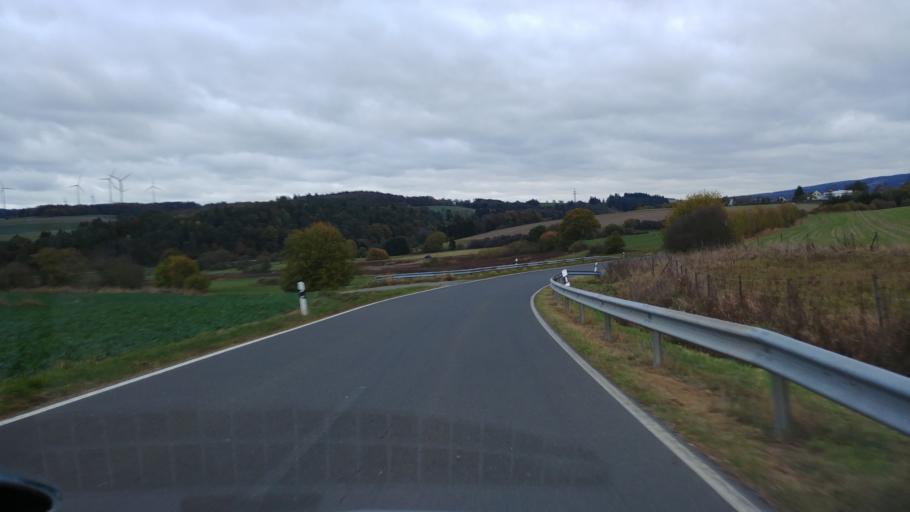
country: DE
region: Rheinland-Pfalz
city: Morbach
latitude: 49.8063
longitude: 7.1058
